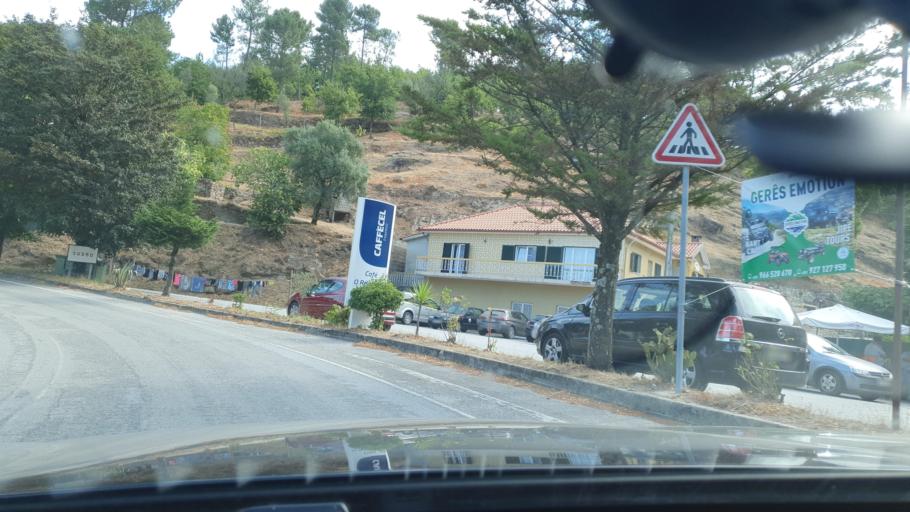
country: PT
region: Braga
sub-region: Vieira do Minho
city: Vieira do Minho
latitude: 41.6775
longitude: -8.1184
